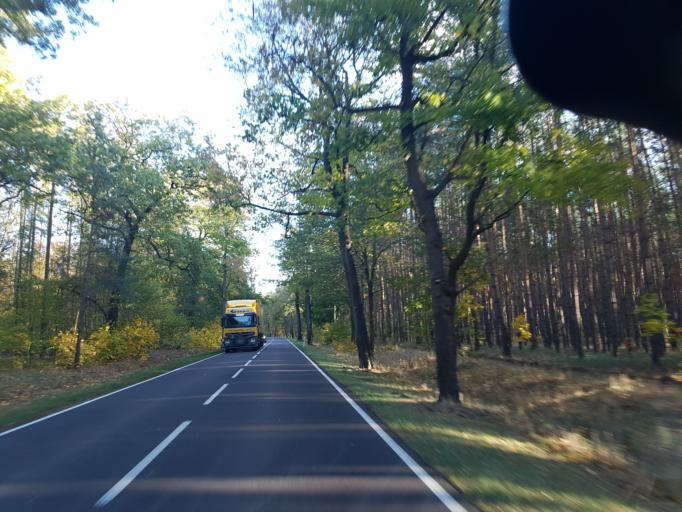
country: DE
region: Brandenburg
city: Brieselang
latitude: 52.6195
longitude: 12.9628
